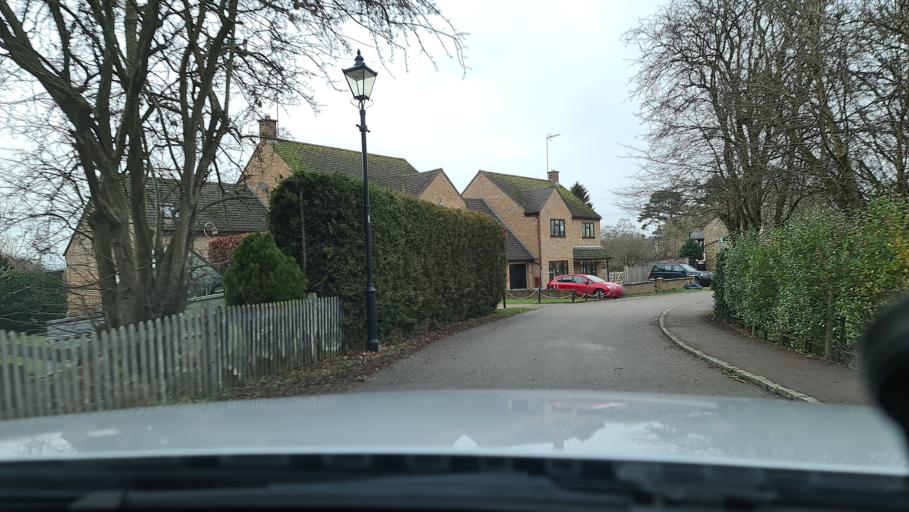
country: GB
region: England
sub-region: Oxfordshire
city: Adderbury
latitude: 52.0213
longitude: -1.2808
